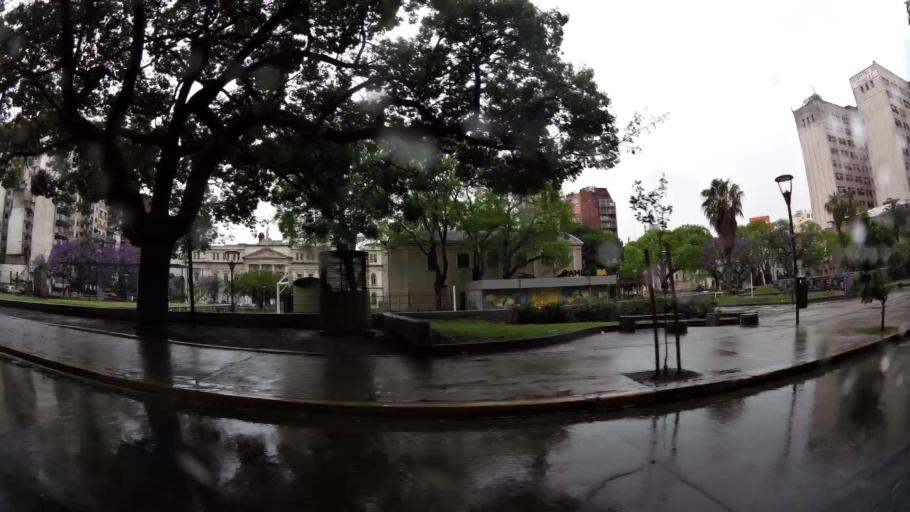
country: AR
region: Buenos Aires F.D.
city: Retiro
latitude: -34.5986
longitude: -58.3979
